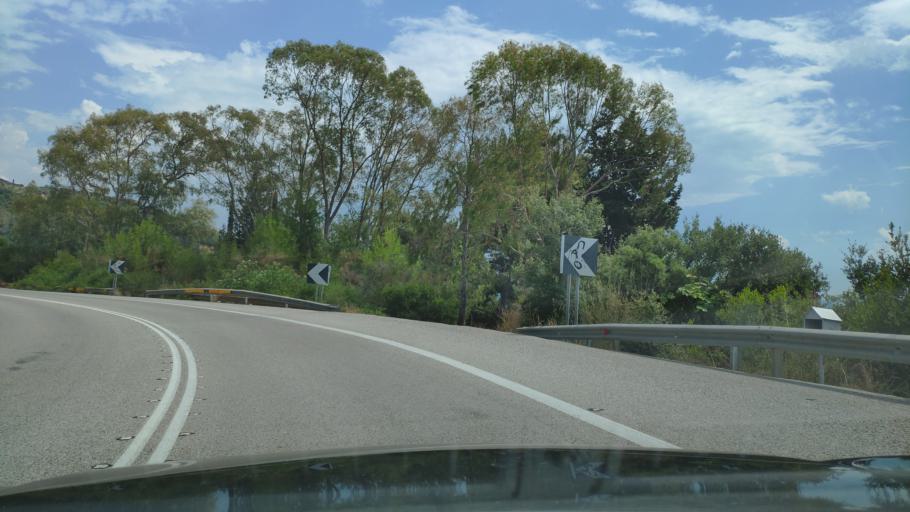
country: GR
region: West Greece
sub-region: Nomos Aitolias kai Akarnanias
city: Menidi
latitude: 39.0345
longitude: 21.1192
